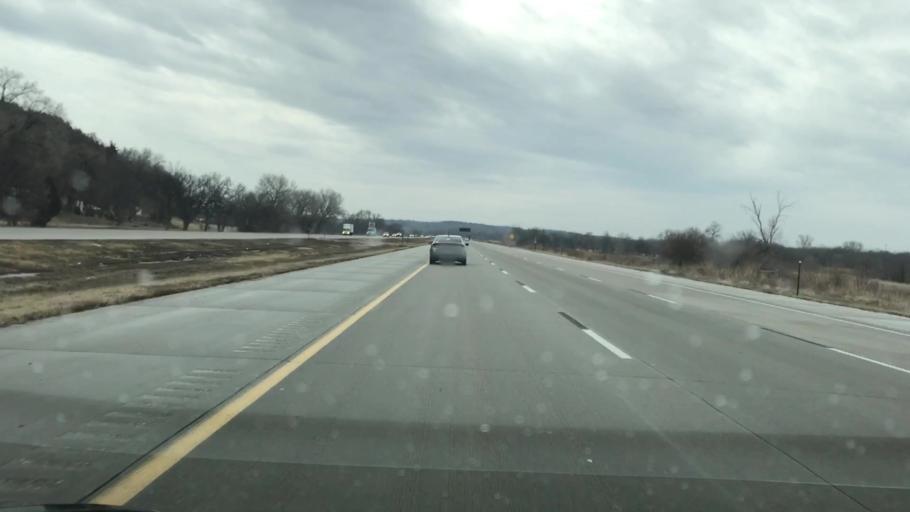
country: US
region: Nebraska
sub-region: Saunders County
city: Ashland
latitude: 41.0462
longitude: -96.2951
